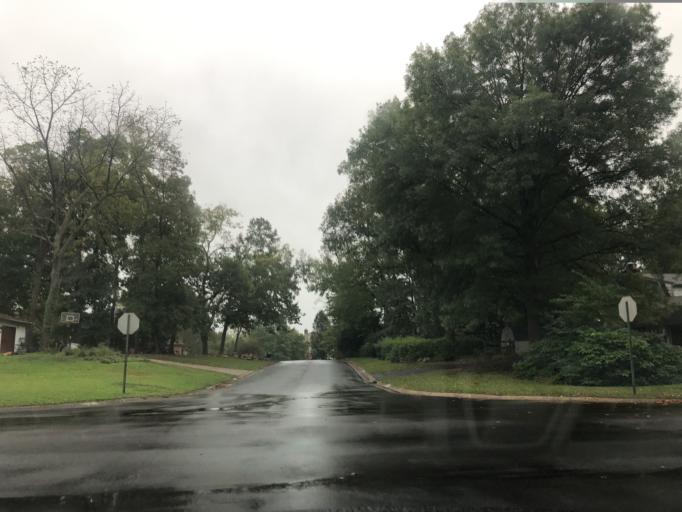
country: US
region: Ohio
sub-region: Hamilton County
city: The Village of Indian Hill
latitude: 39.2667
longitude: -84.2887
